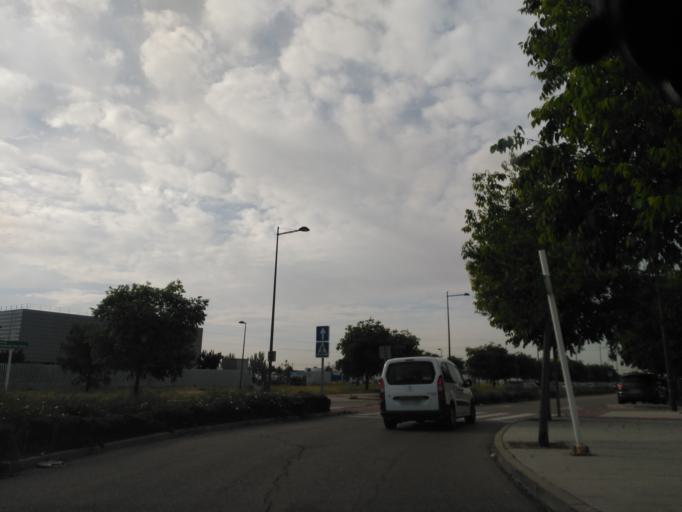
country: ES
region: Madrid
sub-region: Provincia de Madrid
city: Getafe
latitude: 40.2902
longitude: -3.6953
